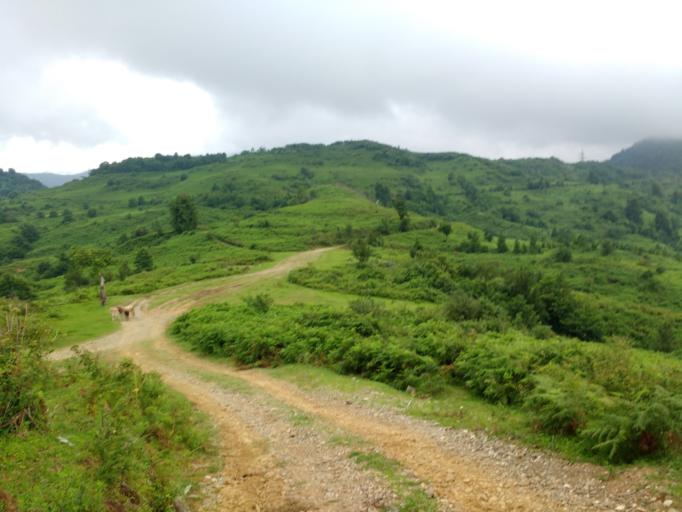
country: GE
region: Ajaria
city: Khelvachauri
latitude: 41.5605
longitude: 41.5846
